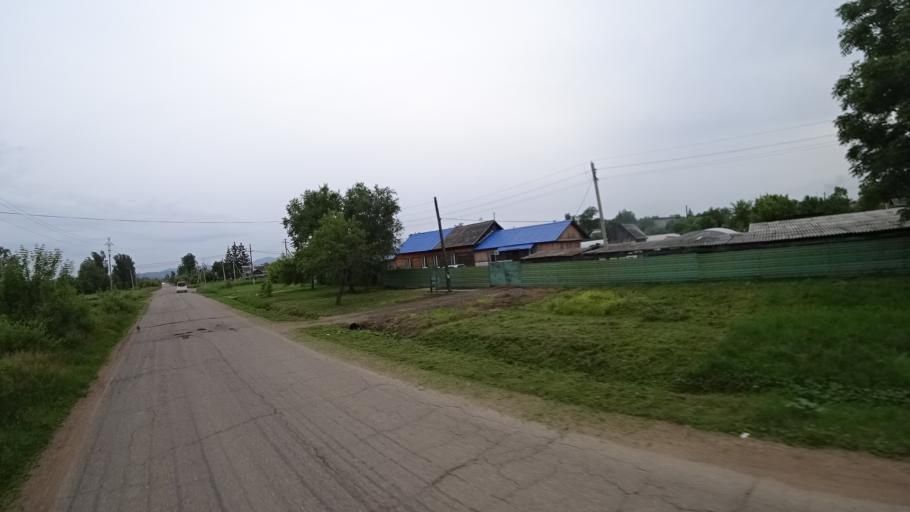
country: RU
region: Primorskiy
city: Novosysoyevka
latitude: 44.2416
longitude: 133.3680
